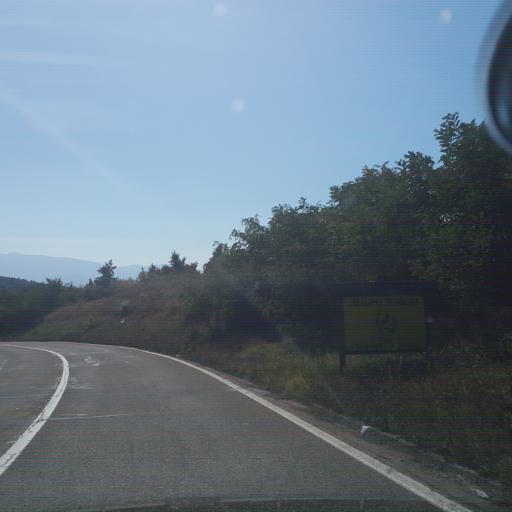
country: RS
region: Central Serbia
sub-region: Zajecarski Okrug
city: Knjazevac
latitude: 43.4746
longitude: 22.2278
